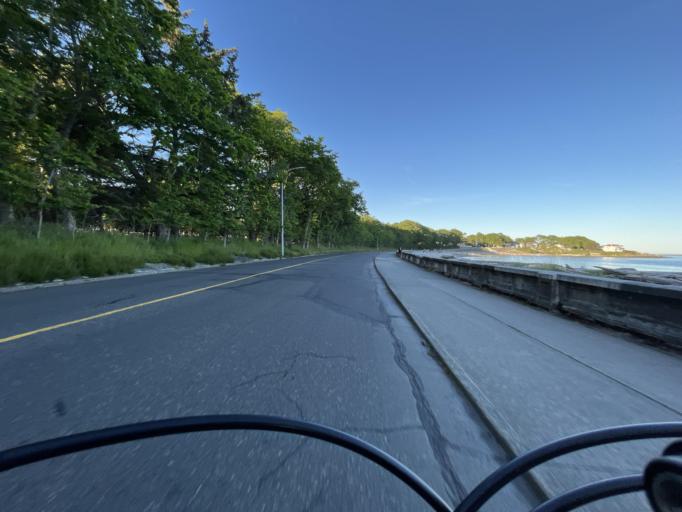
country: CA
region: British Columbia
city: Victoria
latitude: 48.4099
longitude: -123.3419
